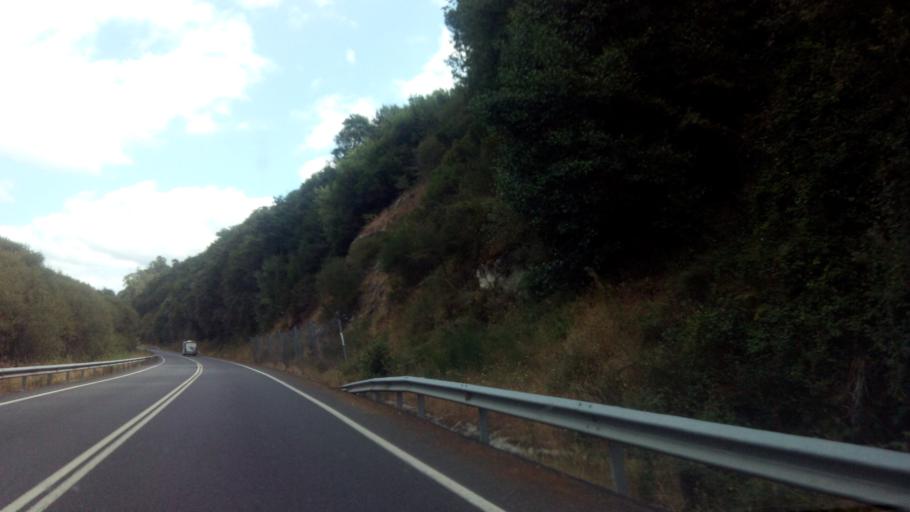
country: ES
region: Galicia
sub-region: Provincia de Ourense
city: Nogueira de Ramuin
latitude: 42.4104
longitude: -7.7850
